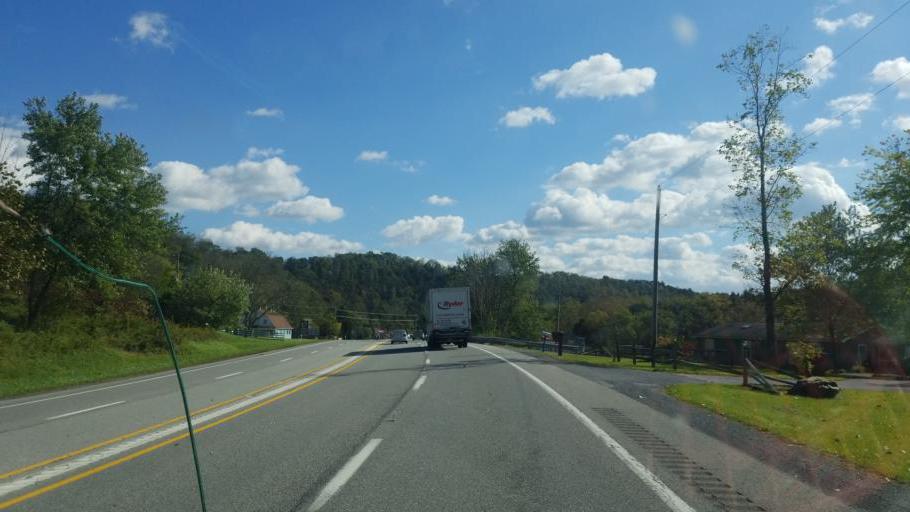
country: US
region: Pennsylvania
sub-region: Bedford County
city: Earlston
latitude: 40.0076
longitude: -78.3105
